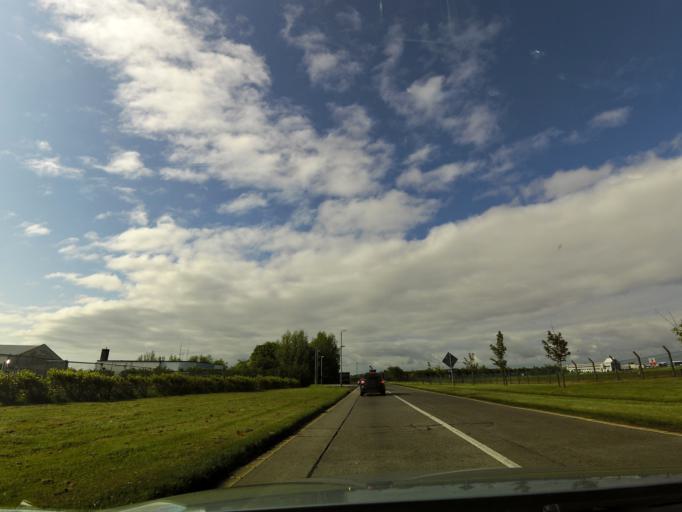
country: IE
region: Munster
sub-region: An Clar
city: Shannon
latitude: 52.6951
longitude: -8.9019
